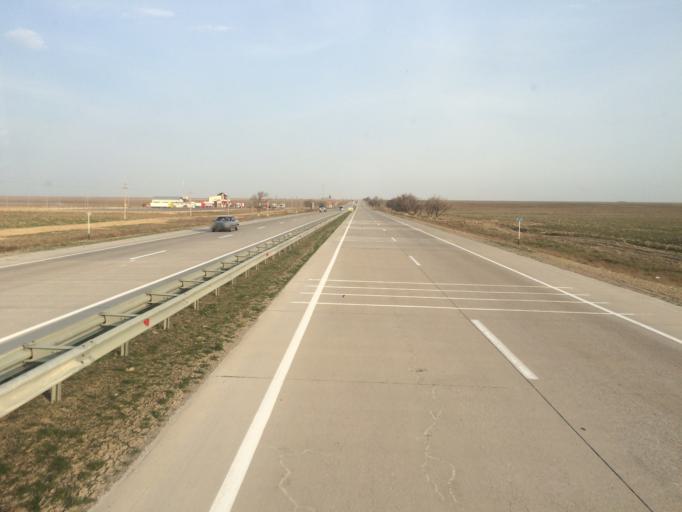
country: KZ
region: Ongtustik Qazaqstan
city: Temirlanovka
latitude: 42.8429
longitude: 69.1006
